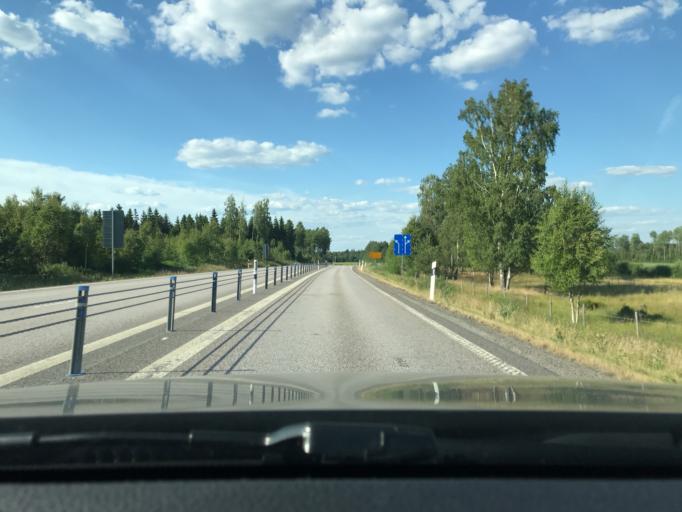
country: SE
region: Kronoberg
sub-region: Alvesta Kommun
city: Vislanda
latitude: 56.7596
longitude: 14.5233
